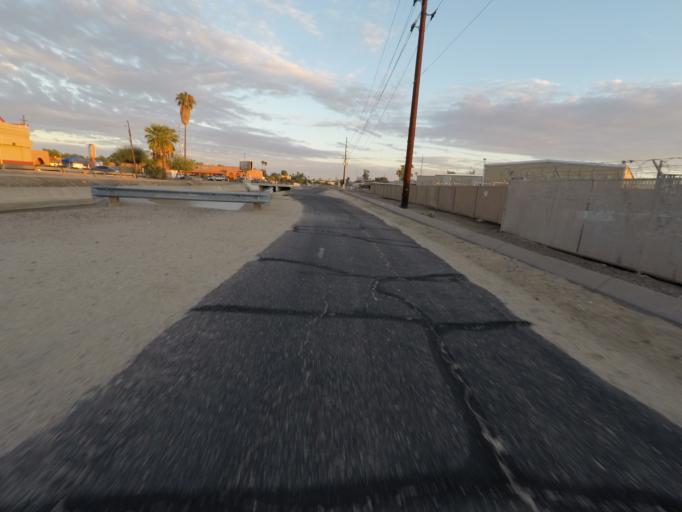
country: US
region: Arizona
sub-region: Maricopa County
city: Phoenix
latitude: 33.4943
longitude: -112.0486
